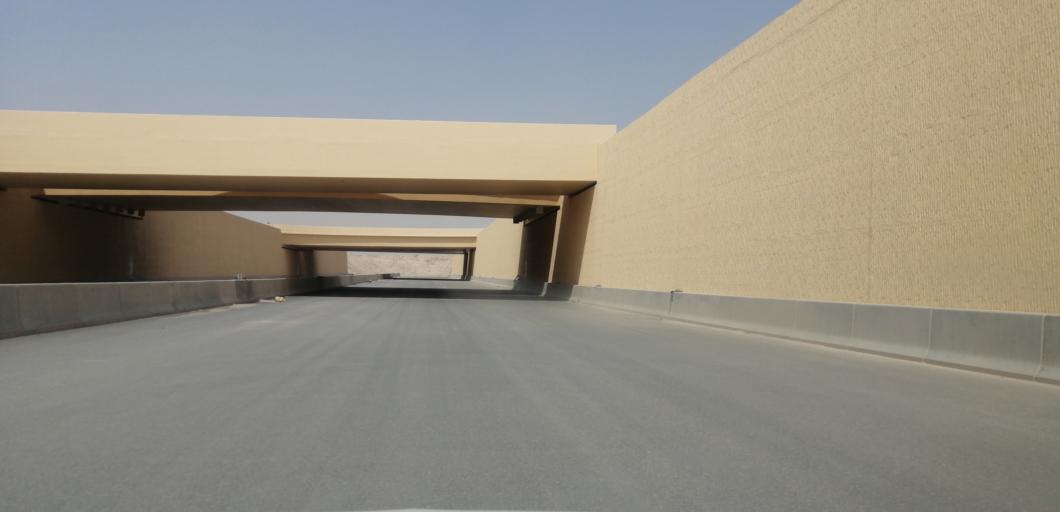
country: KW
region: Muhafazat al Jahra'
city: Al Jahra'
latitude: 29.4539
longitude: 47.5501
